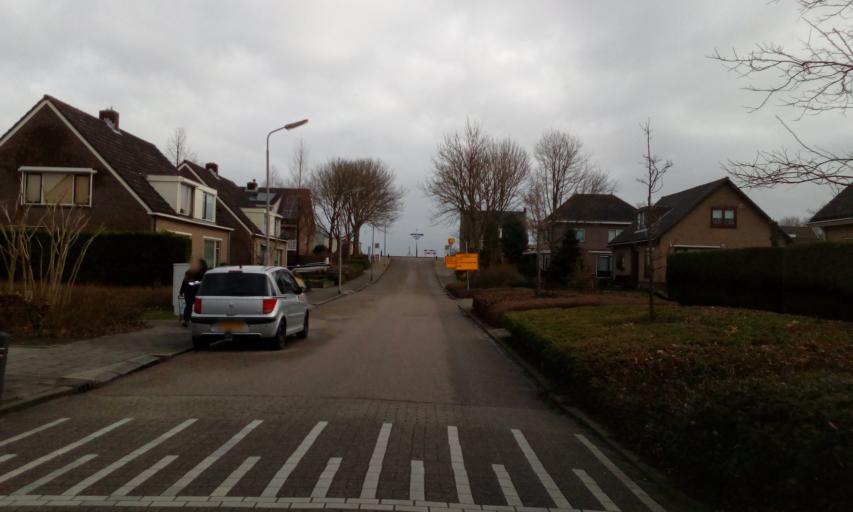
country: NL
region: South Holland
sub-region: Gemeente Nieuwkoop
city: Nieuwkoop
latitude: 52.1920
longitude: 4.7725
